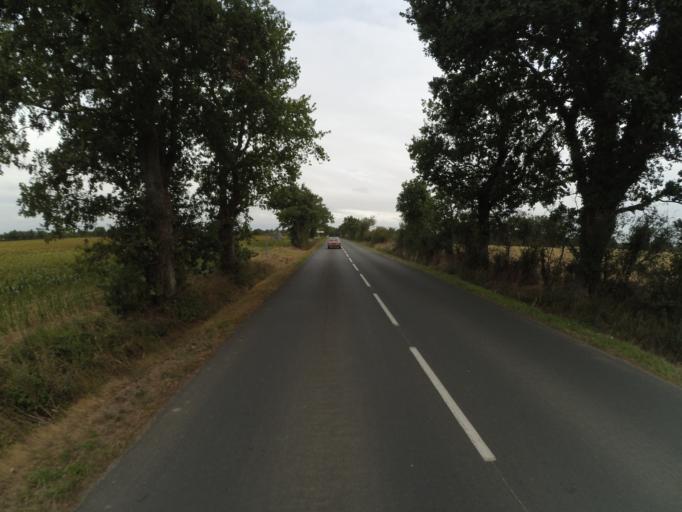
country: FR
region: Pays de la Loire
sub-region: Departement de la Vendee
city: Saint-Andre-Treize-Voies
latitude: 46.9430
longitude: -1.4122
